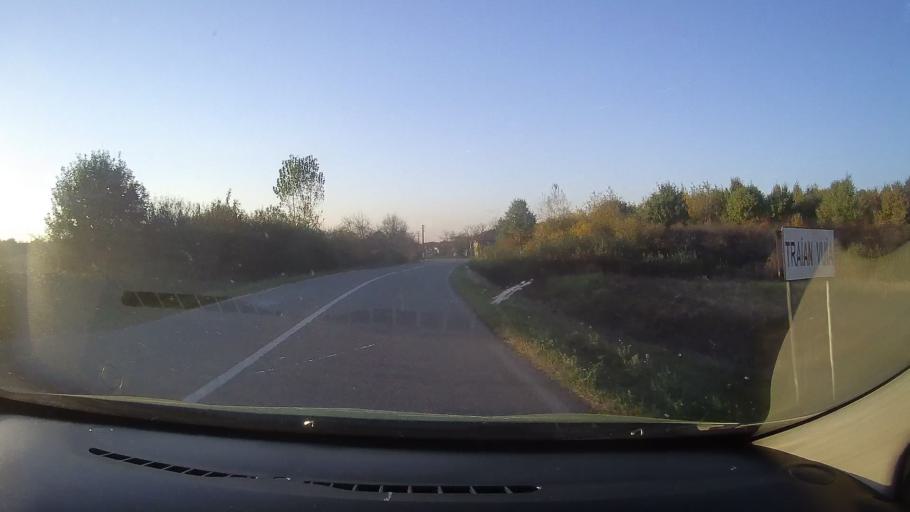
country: RO
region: Timis
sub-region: Comuna Traian Vuia
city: Traian Vuia
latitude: 45.7917
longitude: 22.0730
